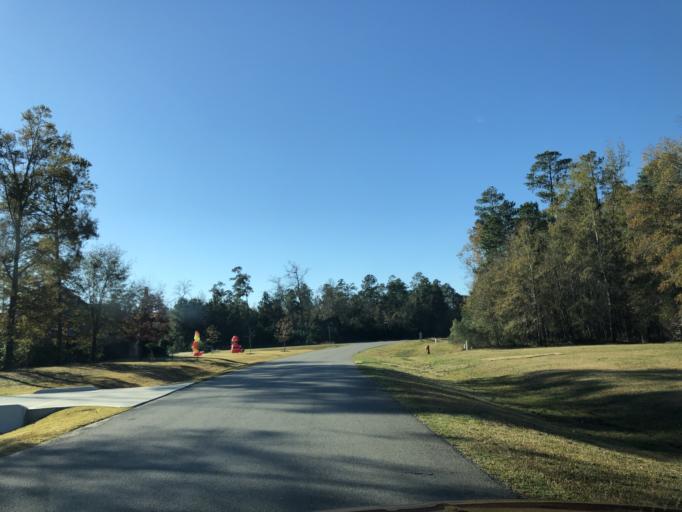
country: US
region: Texas
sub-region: Montgomery County
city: Porter Heights
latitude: 30.0697
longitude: -95.3224
